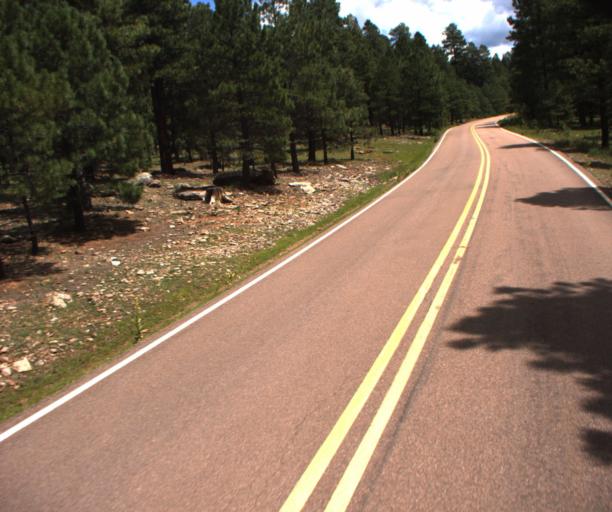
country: US
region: Arizona
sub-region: Navajo County
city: Pinetop-Lakeside
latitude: 34.0050
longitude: -109.7603
